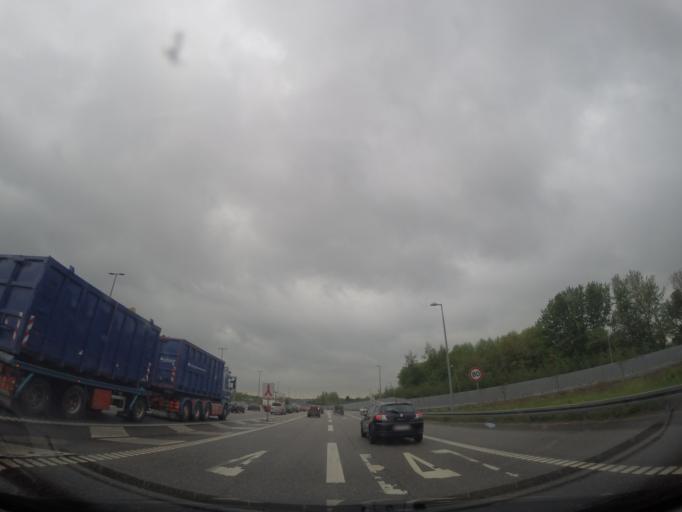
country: DK
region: Capital Region
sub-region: Herlev Kommune
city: Herlev
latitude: 55.7318
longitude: 12.4543
